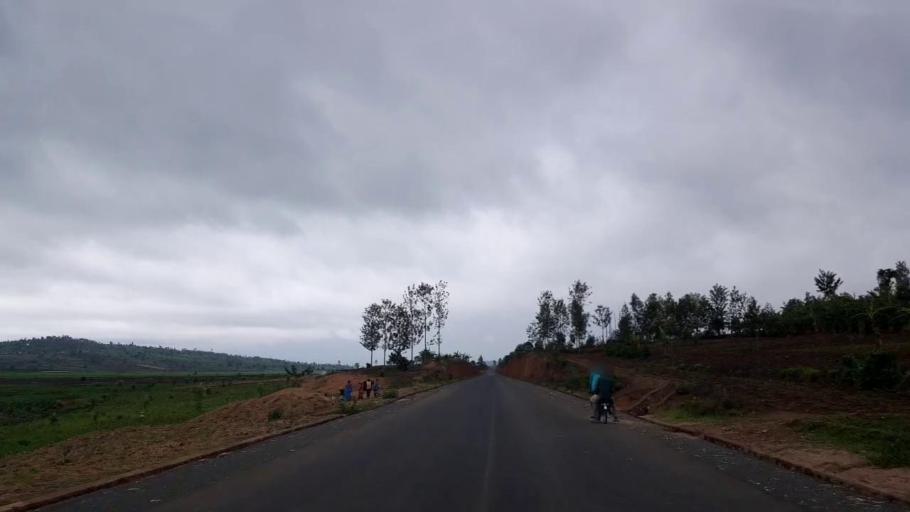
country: RW
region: Northern Province
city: Byumba
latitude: -1.4327
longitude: 30.2616
